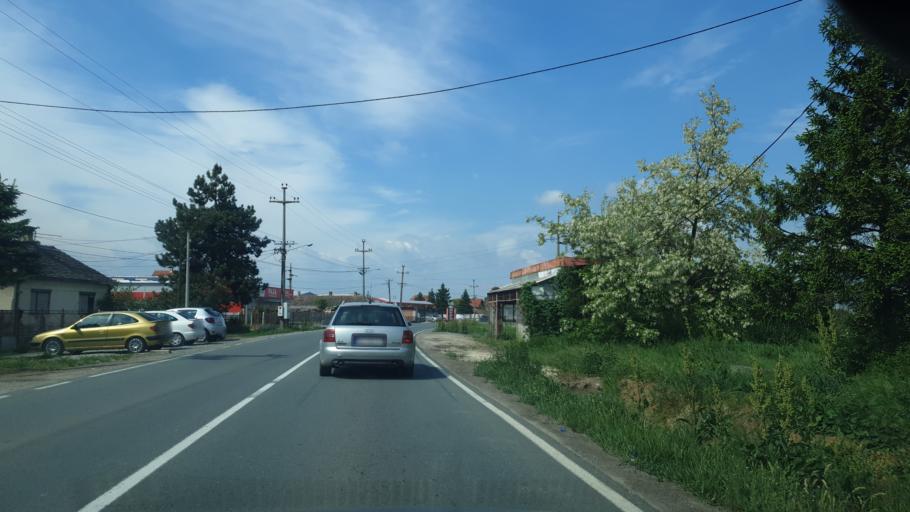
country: RS
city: Zvecka
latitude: 44.6418
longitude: 20.1834
